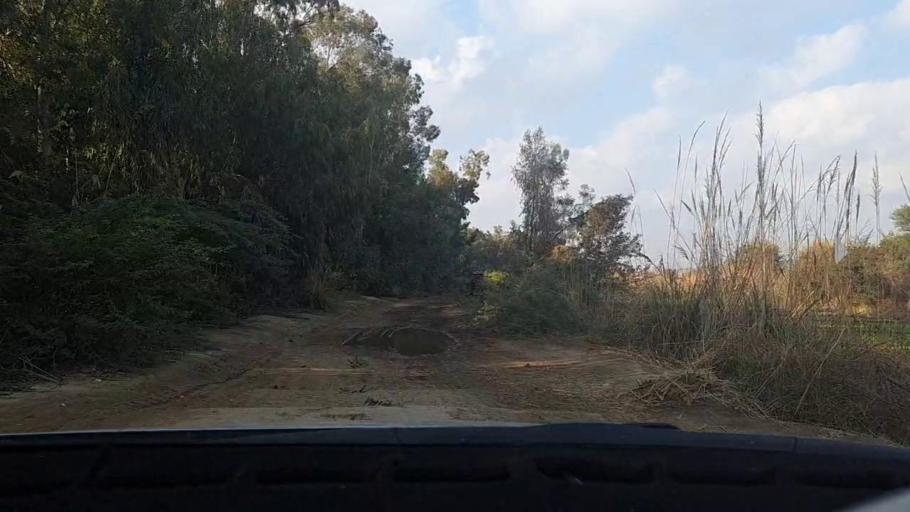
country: PK
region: Sindh
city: Tando Mittha Khan
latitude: 25.9130
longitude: 69.3029
